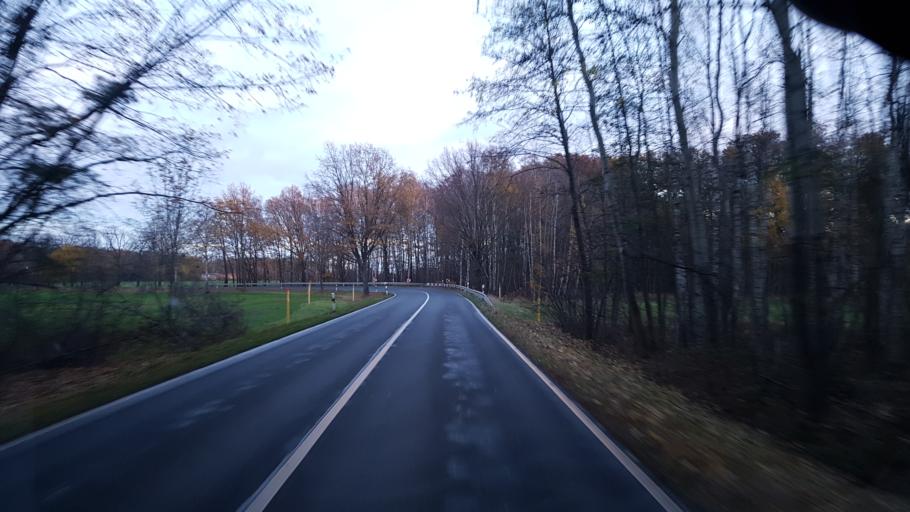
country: DE
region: Brandenburg
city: Schraden
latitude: 51.4436
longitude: 13.7091
